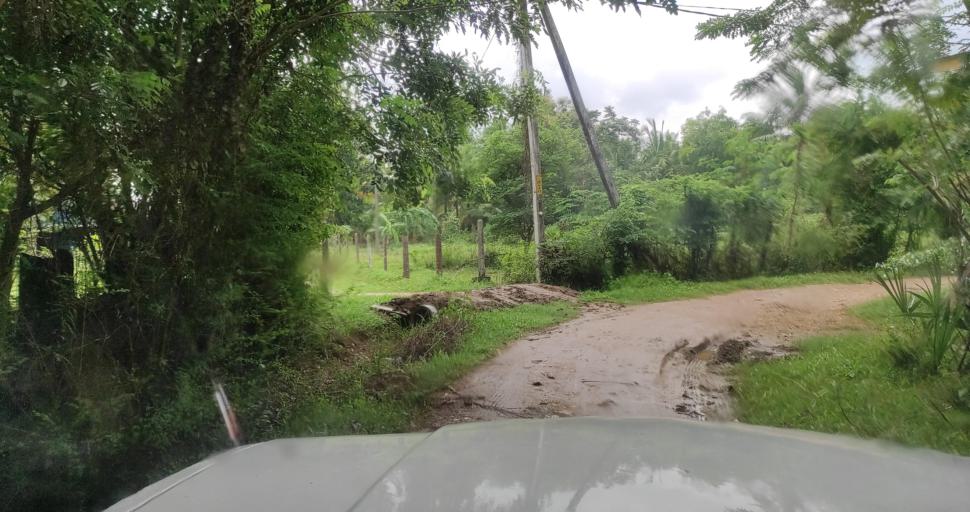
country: LK
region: Eastern Province
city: Trincomalee
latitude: 8.3718
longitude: 81.0157
